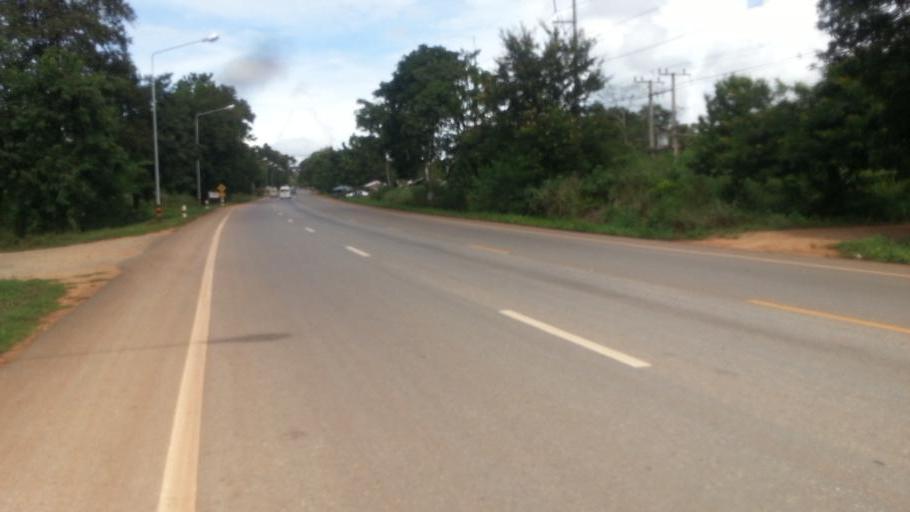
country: TH
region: Kanchanaburi
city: Sai Yok
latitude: 14.1147
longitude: 99.1902
